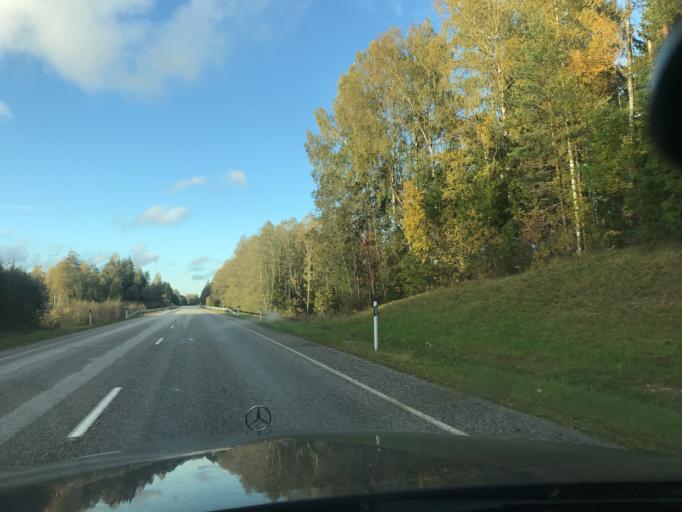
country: RU
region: Pskov
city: Pechory
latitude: 57.6706
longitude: 27.3287
